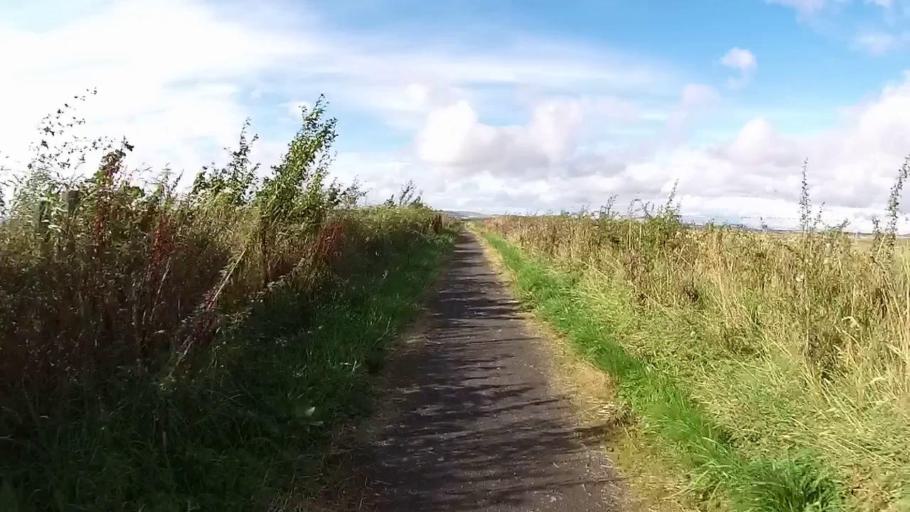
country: GB
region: Scotland
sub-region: Fife
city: Kelty
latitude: 56.1750
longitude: -3.3827
